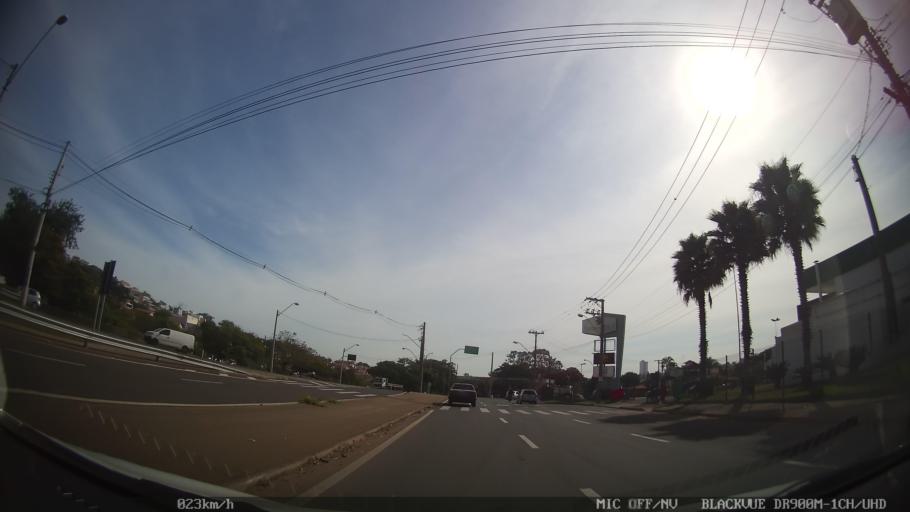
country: BR
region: Sao Paulo
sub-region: Piracicaba
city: Piracicaba
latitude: -22.7412
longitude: -47.6685
